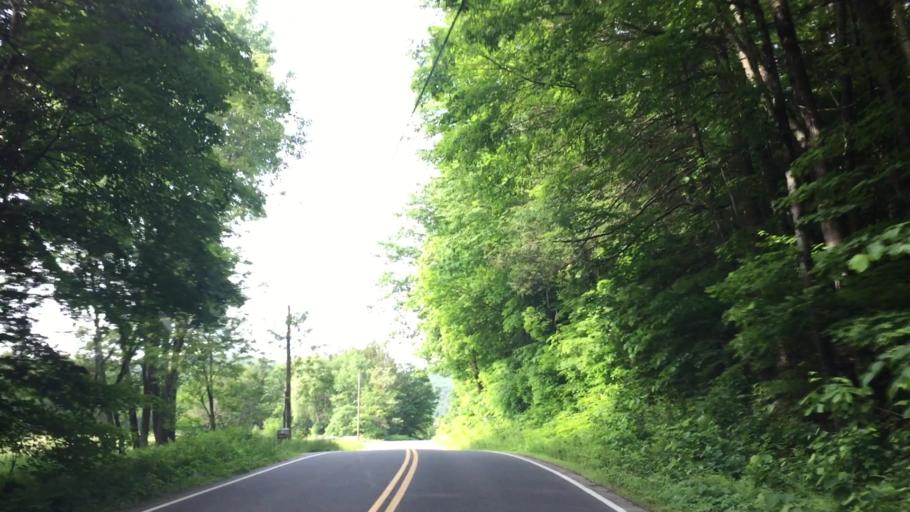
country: US
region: Massachusetts
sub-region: Hampshire County
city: Westhampton
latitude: 42.2462
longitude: -72.8794
